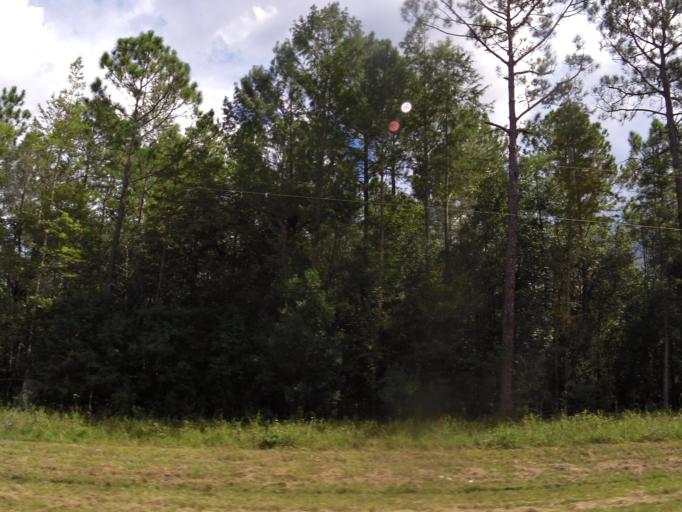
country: US
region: Georgia
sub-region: Brantley County
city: Nahunta
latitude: 31.0483
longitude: -82.0178
